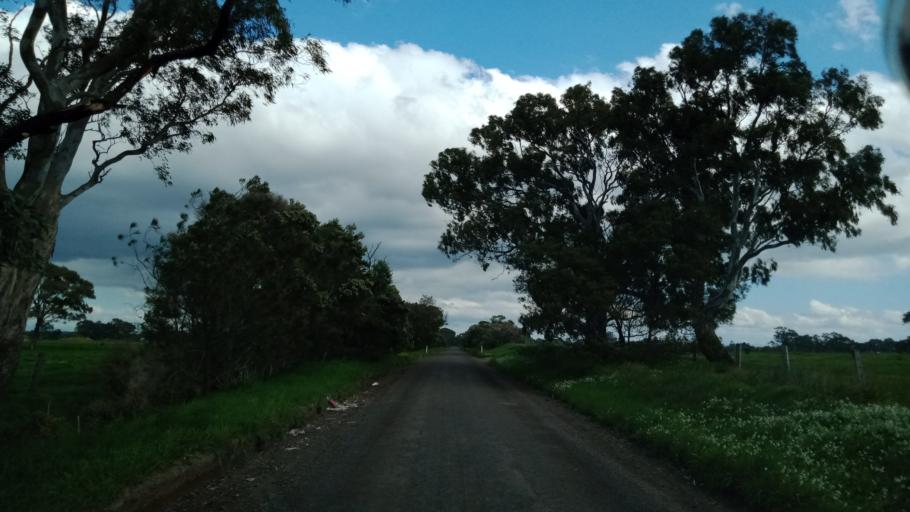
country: AU
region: Victoria
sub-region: Frankston
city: Skye
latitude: -38.0963
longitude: 145.2171
